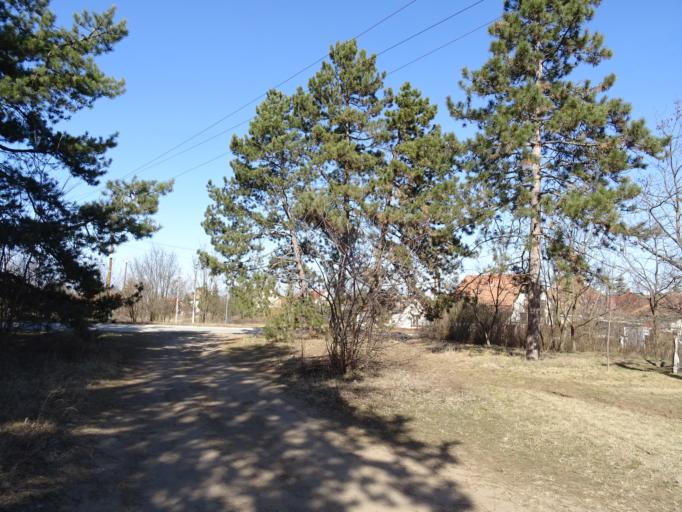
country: HU
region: Pest
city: Veresegyhaz
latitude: 47.6428
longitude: 19.2805
